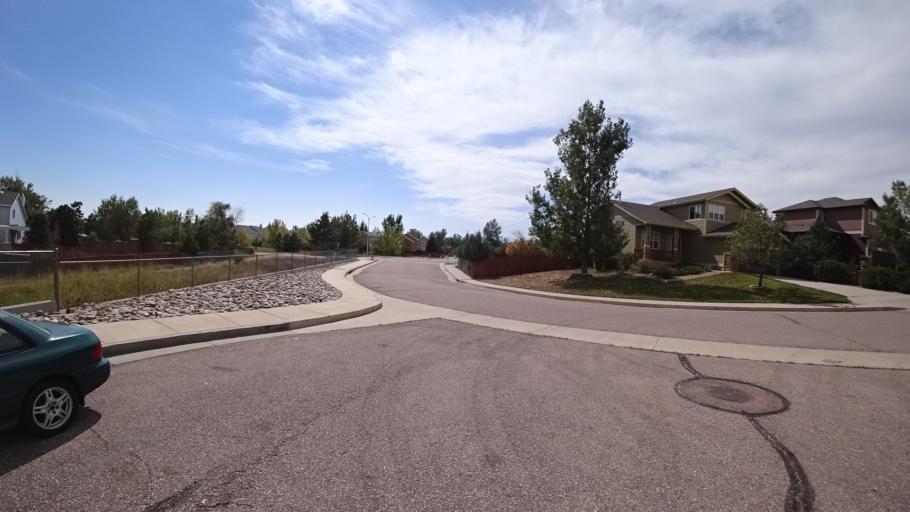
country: US
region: Colorado
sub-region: El Paso County
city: Cimarron Hills
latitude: 38.9075
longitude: -104.7080
